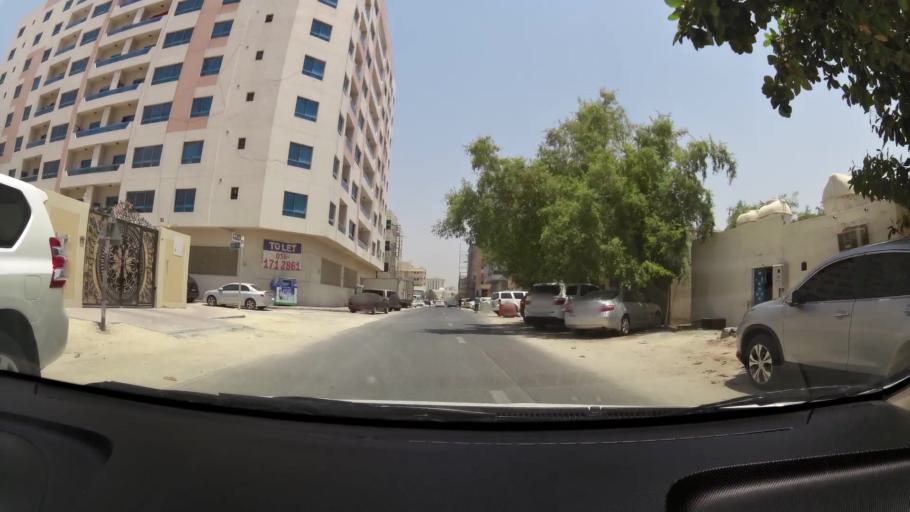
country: AE
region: Ajman
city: Ajman
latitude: 25.4043
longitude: 55.4369
